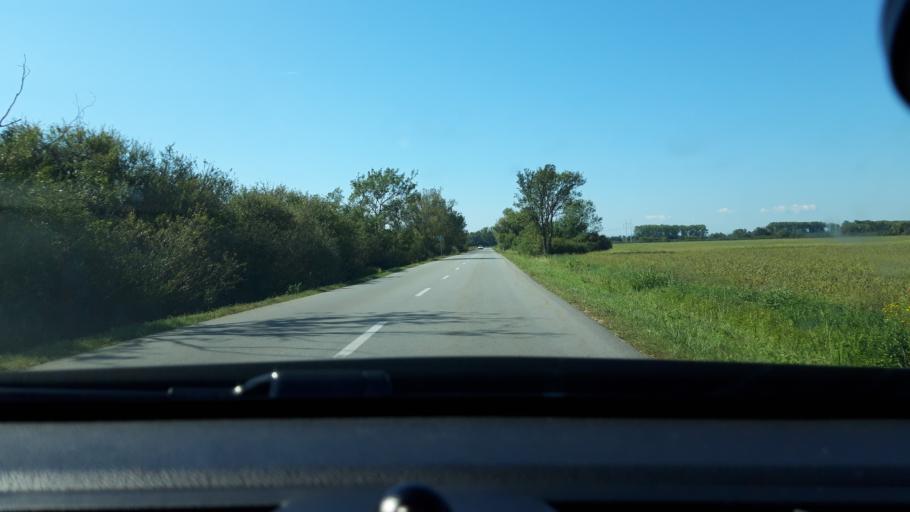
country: SK
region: Kosicky
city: Michalovce
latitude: 48.6487
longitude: 21.9368
